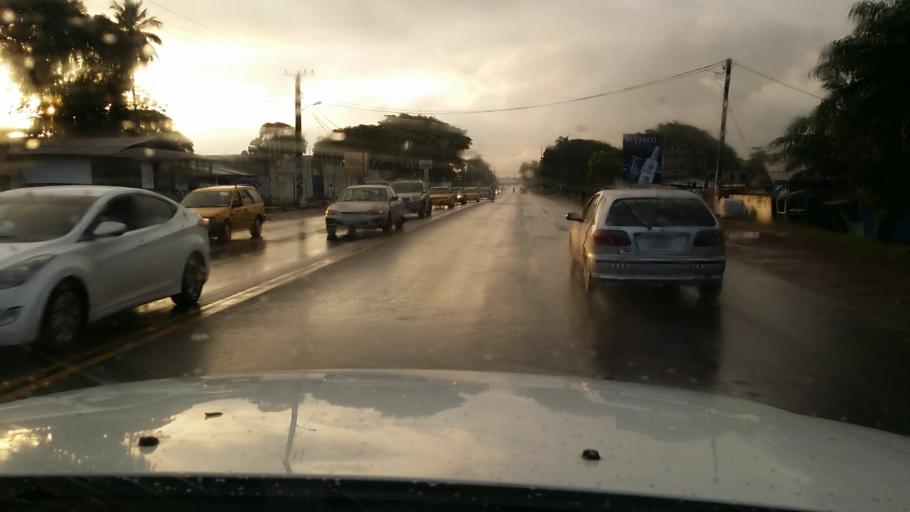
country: LR
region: Montserrado
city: Monrovia
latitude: 6.2677
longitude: -10.7241
